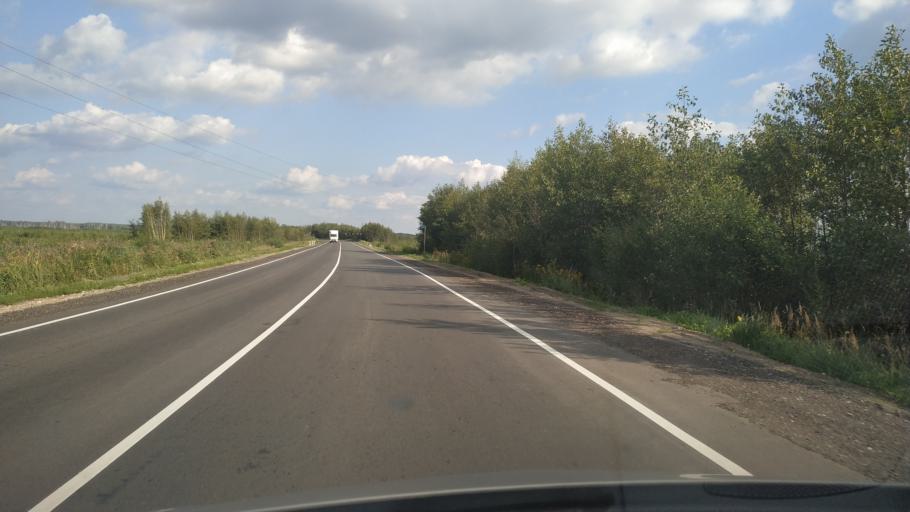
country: RU
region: Moskovskaya
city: Vereya
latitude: 55.7240
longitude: 39.0492
